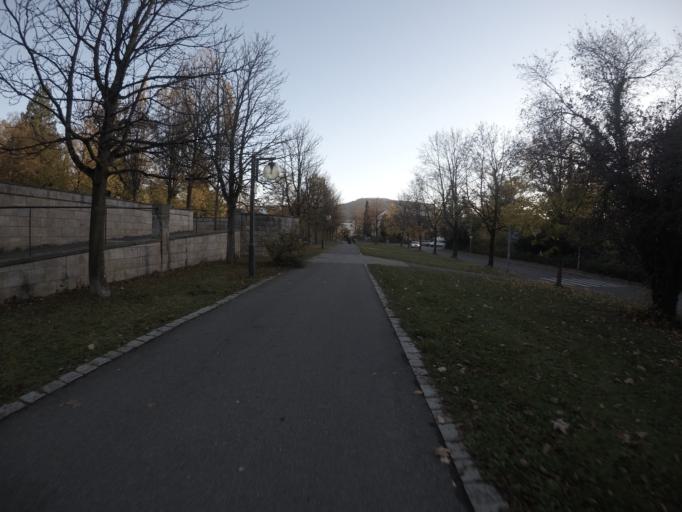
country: DE
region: Baden-Wuerttemberg
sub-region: Tuebingen Region
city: Pfullingen
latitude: 48.4670
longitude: 9.2288
